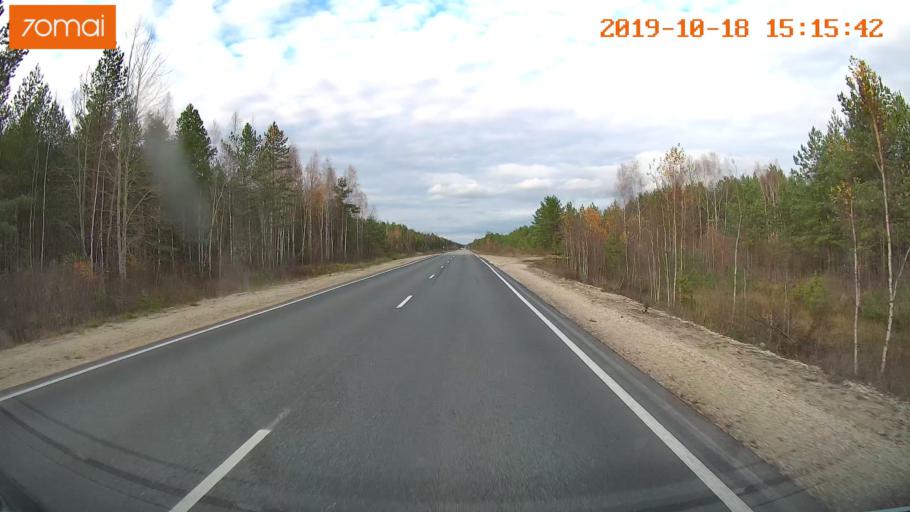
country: RU
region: Vladimir
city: Gus'-Khrustal'nyy
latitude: 55.6236
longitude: 40.7231
